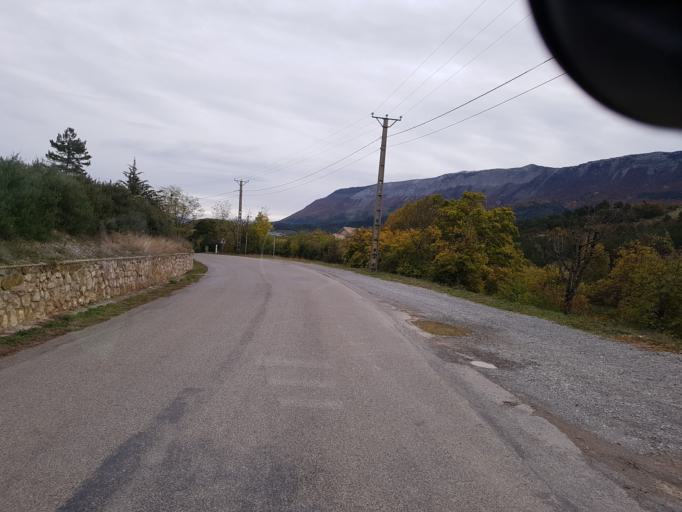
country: FR
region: Provence-Alpes-Cote d'Azur
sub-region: Departement des Hautes-Alpes
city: Laragne-Monteglin
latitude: 44.3154
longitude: 5.7097
